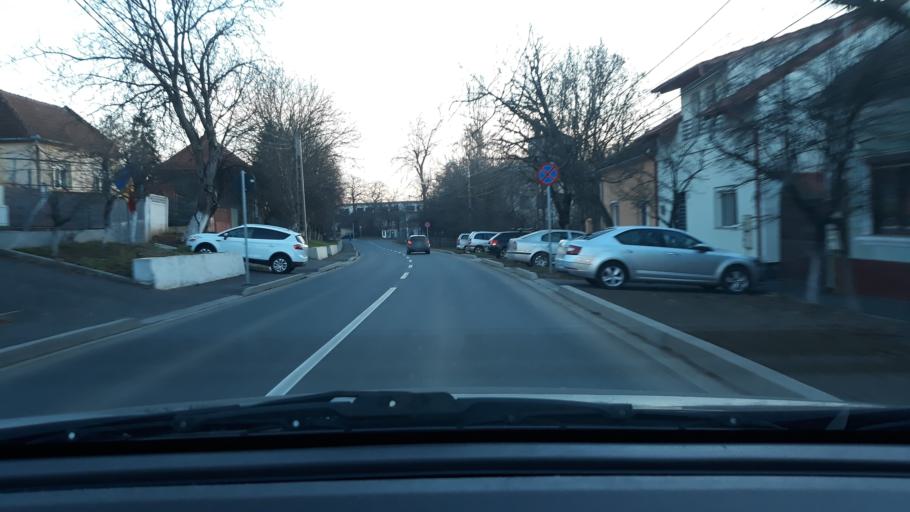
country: RO
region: Bihor
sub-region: Comuna Biharea
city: Oradea
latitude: 47.0837
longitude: 21.9272
